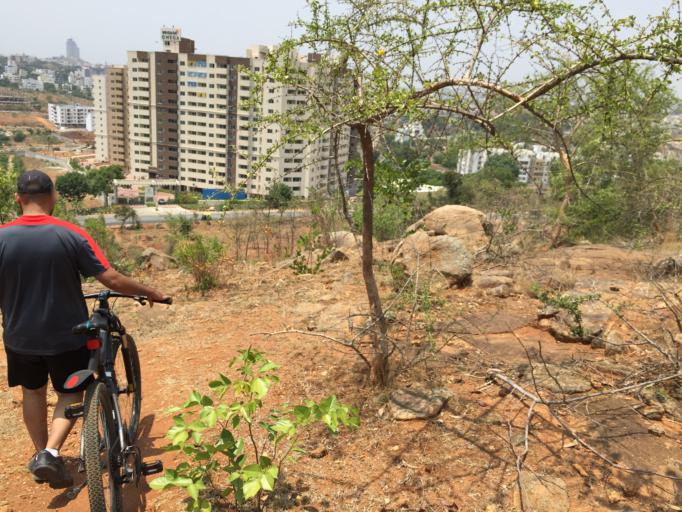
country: IN
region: Karnataka
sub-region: Bangalore Urban
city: Bangalore
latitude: 12.8916
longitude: 77.5284
